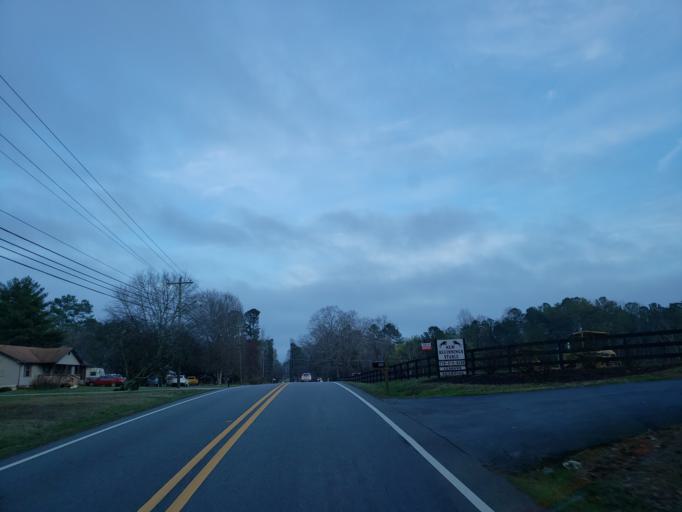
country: US
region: Georgia
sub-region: Cherokee County
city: Ball Ground
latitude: 34.2392
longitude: -84.3473
